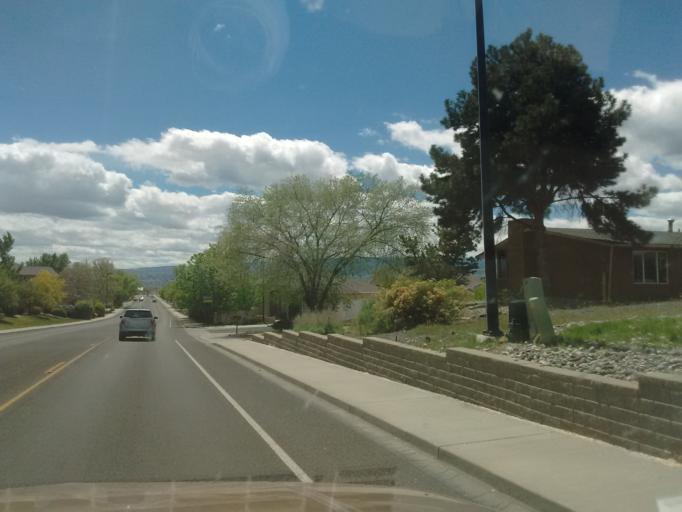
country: US
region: Colorado
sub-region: Mesa County
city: Grand Junction
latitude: 39.0981
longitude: -108.5431
